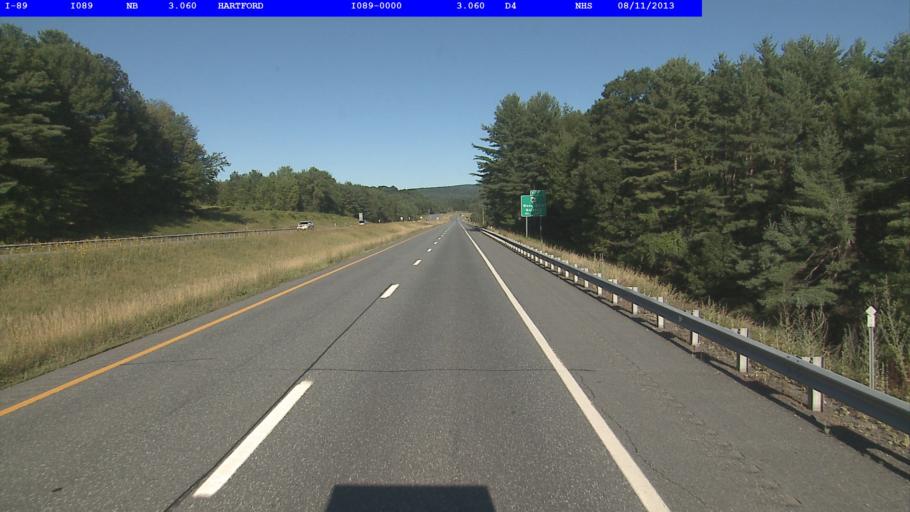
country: US
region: Vermont
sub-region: Windsor County
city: White River Junction
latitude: 43.6621
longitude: -72.3697
